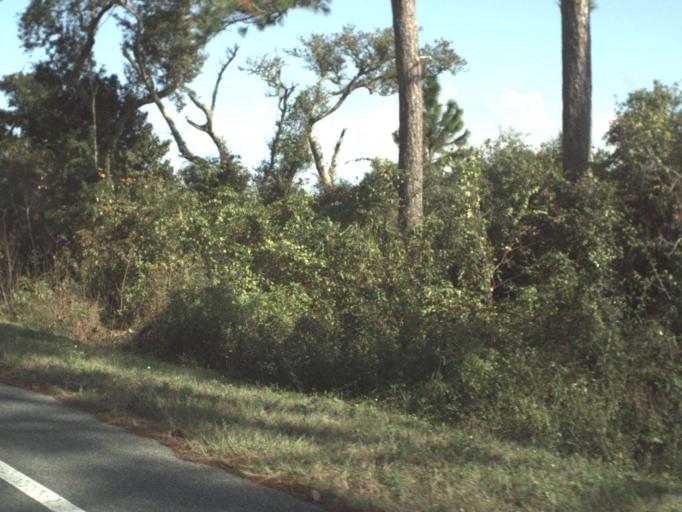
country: US
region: Florida
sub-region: Franklin County
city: Eastpoint
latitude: 29.7783
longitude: -84.7836
